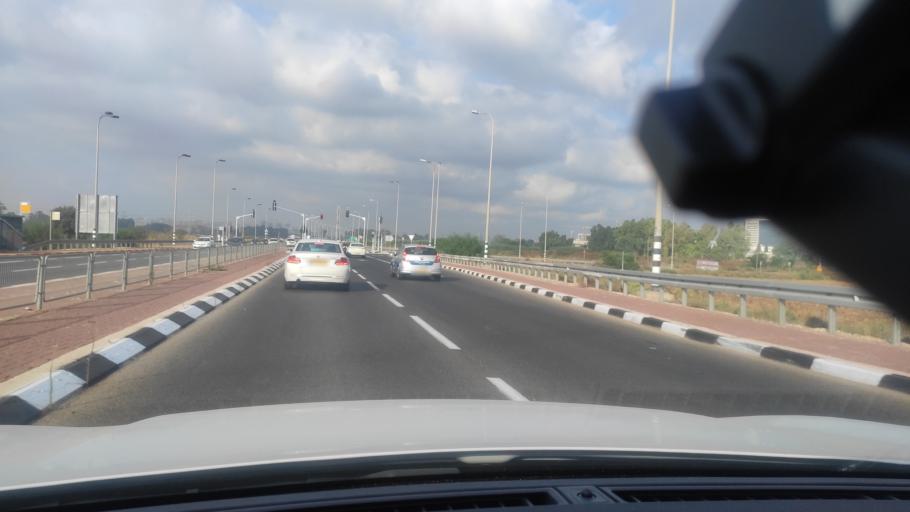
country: IL
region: Central District
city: Hod HaSharon
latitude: 32.1347
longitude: 34.9106
